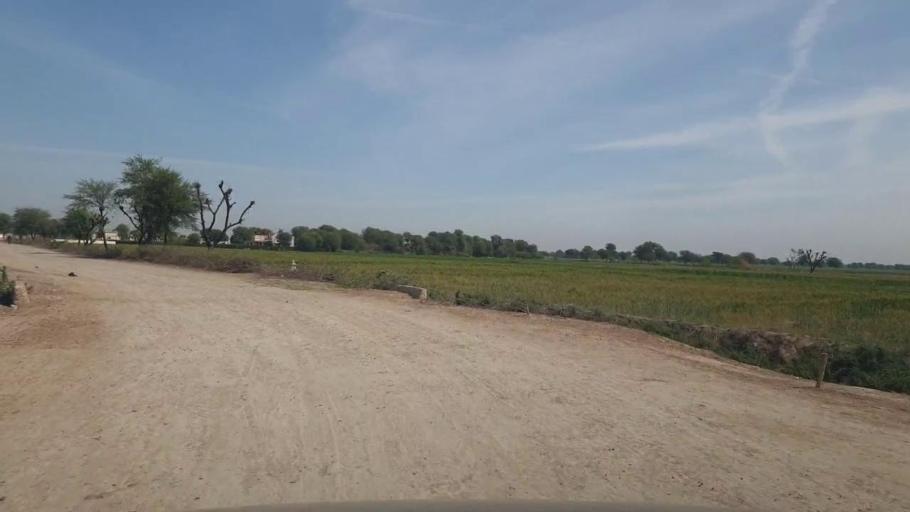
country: PK
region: Sindh
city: Umarkot
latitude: 25.3299
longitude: 69.6156
